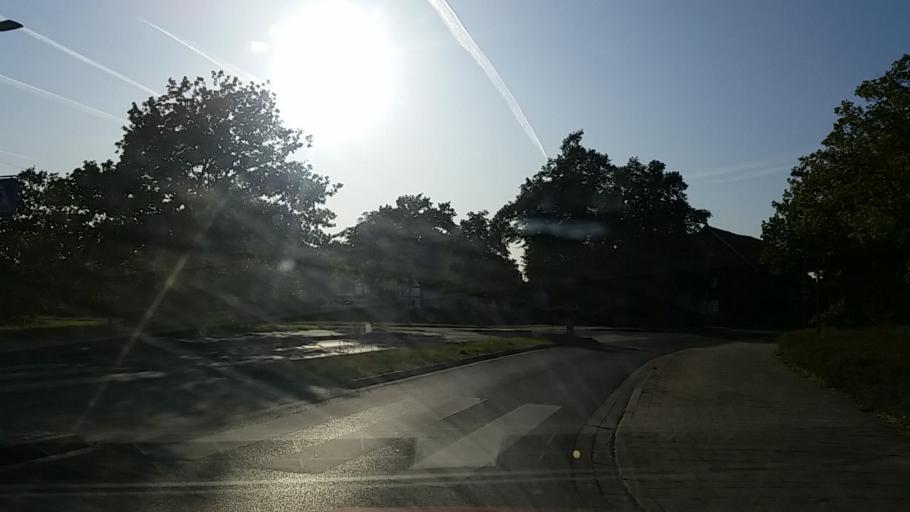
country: DE
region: Lower Saxony
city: Braunschweig
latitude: 52.2971
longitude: 10.5608
